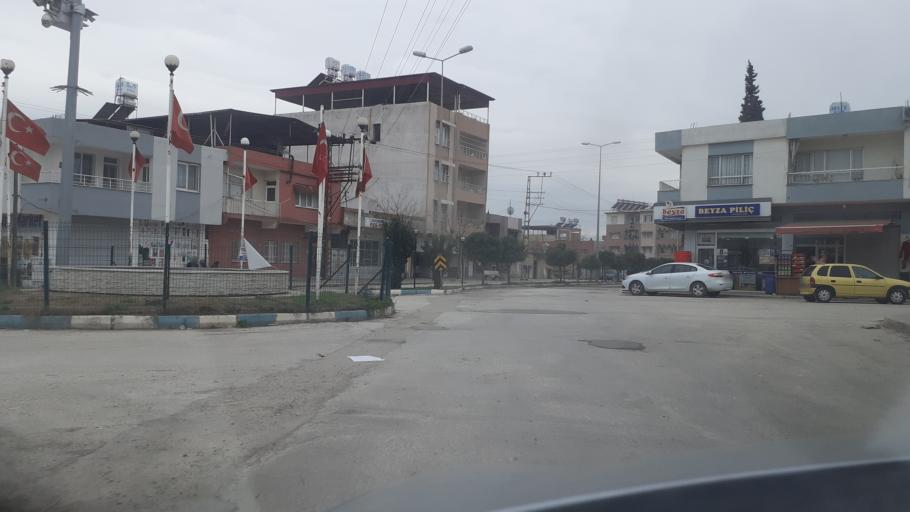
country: TR
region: Hatay
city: Kirikhan
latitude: 36.4914
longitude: 36.3571
